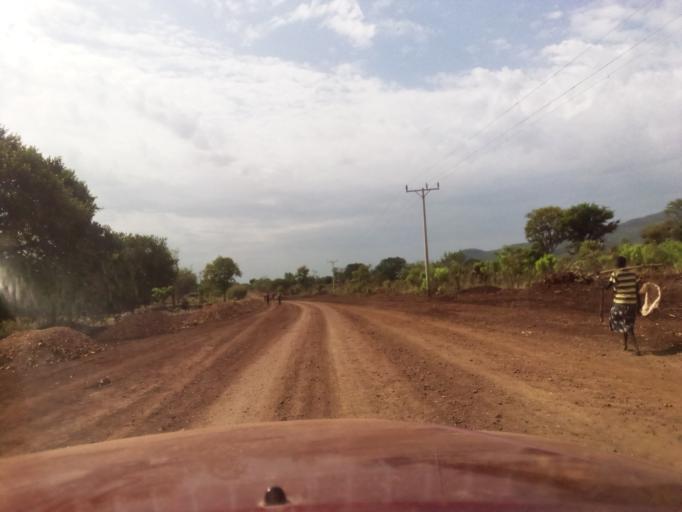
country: ET
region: Oromiya
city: Mendi
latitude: 10.0565
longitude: 35.2867
